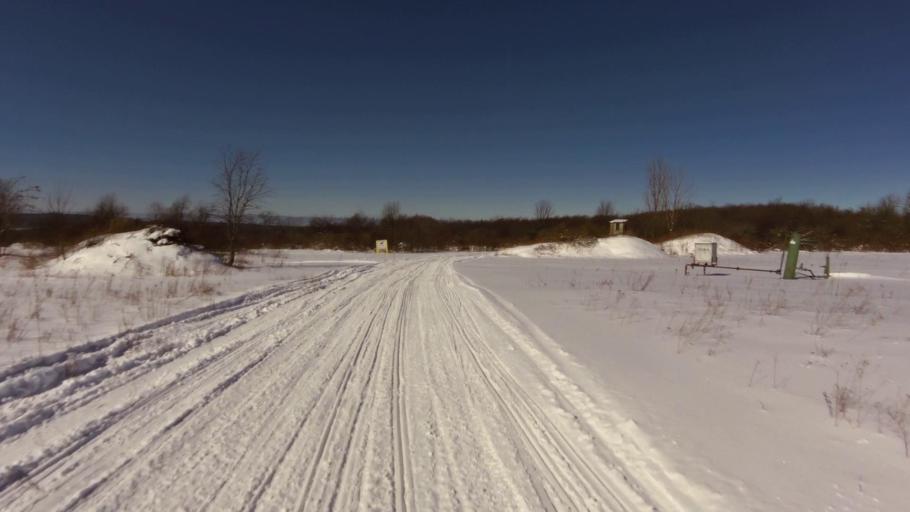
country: US
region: New York
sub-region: Chautauqua County
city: Mayville
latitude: 42.2670
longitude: -79.4530
